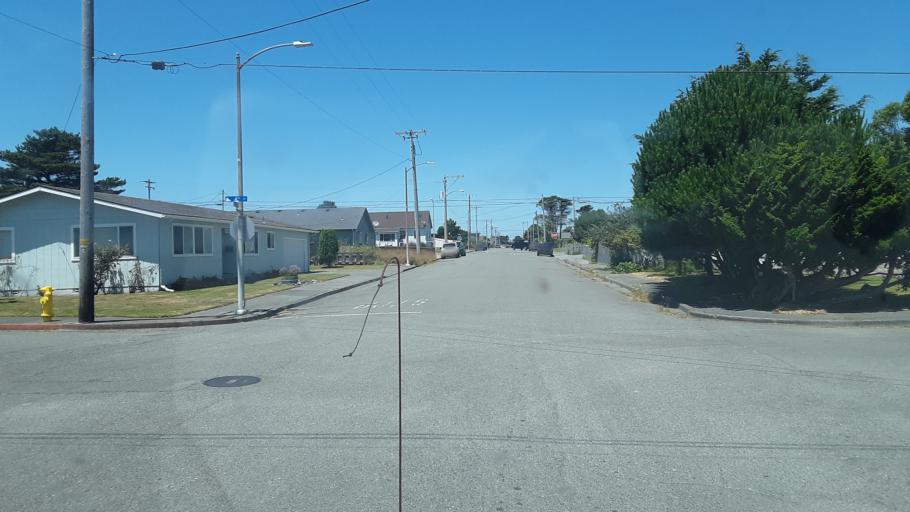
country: US
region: California
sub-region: Del Norte County
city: Crescent City
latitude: 41.7499
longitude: -124.2037
